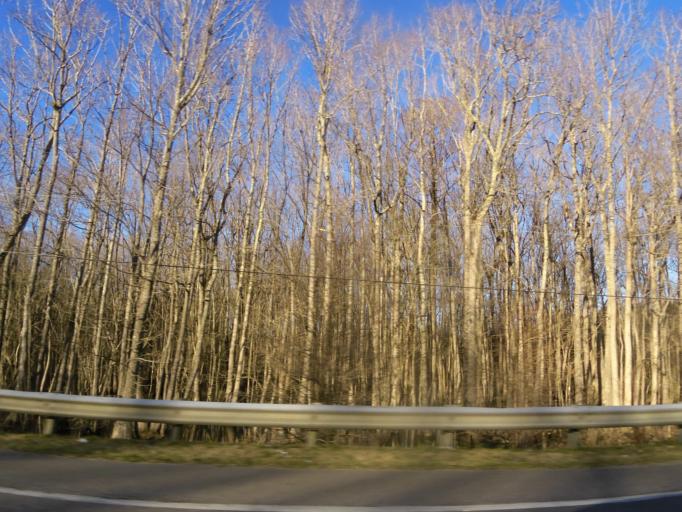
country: US
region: Virginia
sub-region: Isle of Wight County
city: Windsor
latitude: 36.6953
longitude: -76.7261
